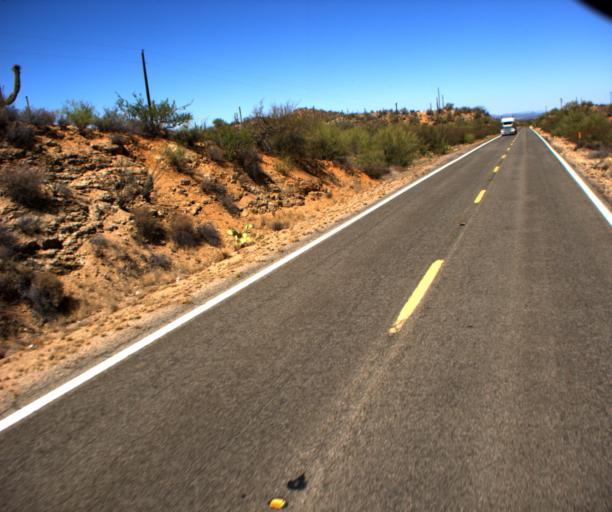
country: US
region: Arizona
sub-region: Pima County
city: Sells
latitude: 32.1745
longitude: -112.1762
